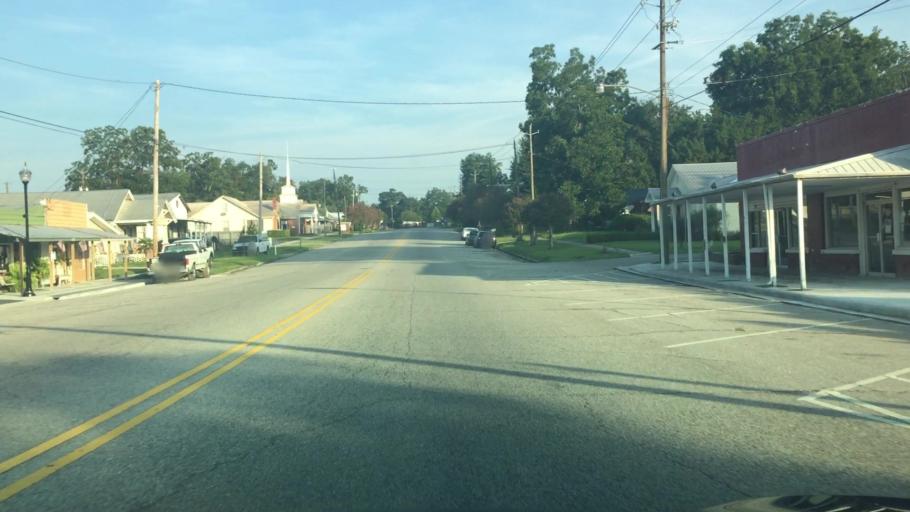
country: US
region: Alabama
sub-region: Covington County
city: Florala
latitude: 31.0072
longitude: -86.3309
